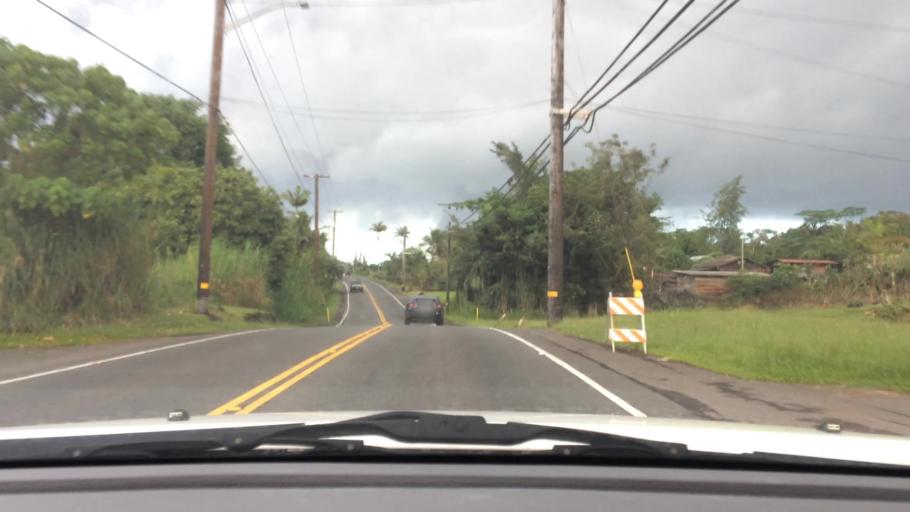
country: US
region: Hawaii
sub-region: Hawaii County
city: Hawaiian Paradise Park
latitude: 19.4972
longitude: -154.9520
